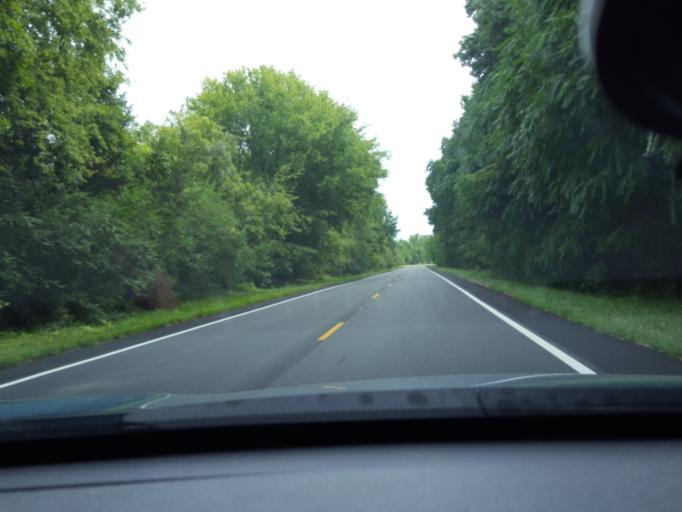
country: US
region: Virginia
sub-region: Hanover County
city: Hanover
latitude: 37.7948
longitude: -77.3708
